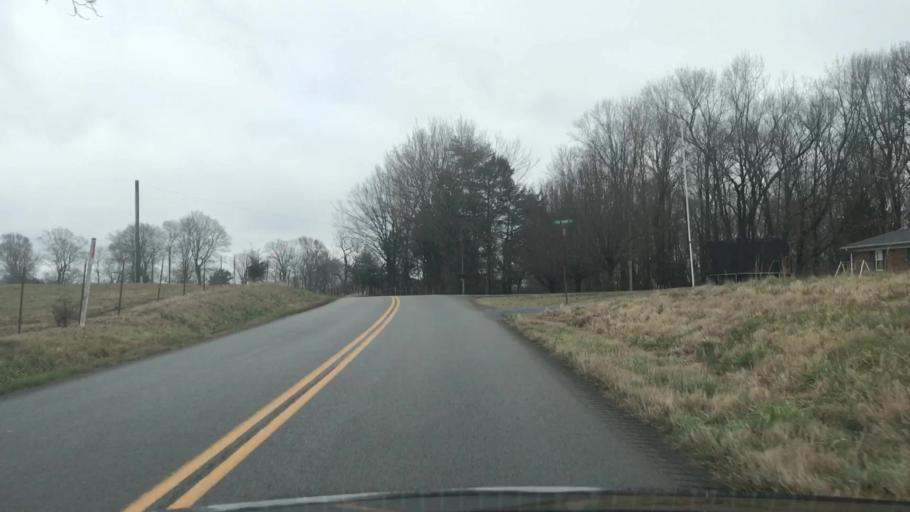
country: US
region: Kentucky
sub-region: Monroe County
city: Tompkinsville
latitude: 36.7544
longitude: -85.7204
